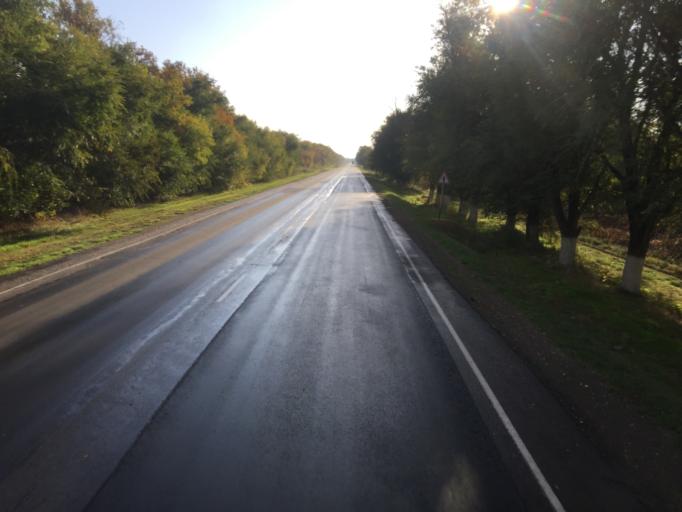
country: RU
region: Rostov
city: Zernograd
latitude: 46.8076
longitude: 40.3234
